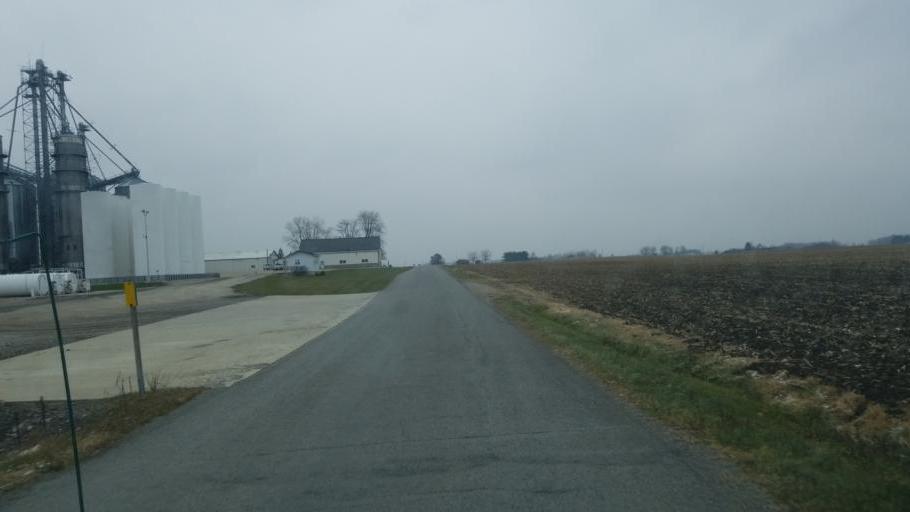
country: US
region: Ohio
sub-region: Richland County
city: Shelby
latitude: 40.8614
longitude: -82.7295
